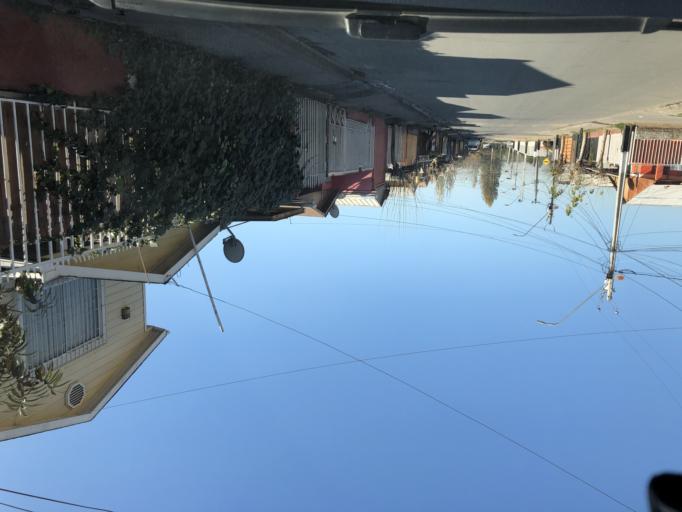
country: CL
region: Santiago Metropolitan
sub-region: Provincia de Santiago
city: La Pintana
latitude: -33.6143
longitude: -70.6243
